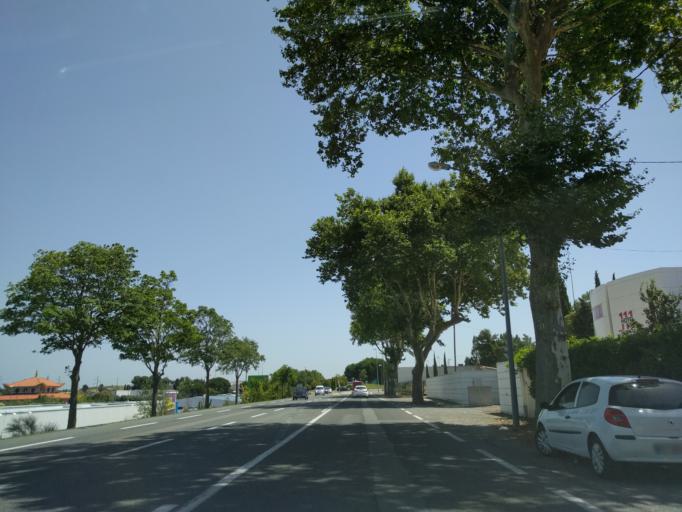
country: FR
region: Languedoc-Roussillon
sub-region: Departement de l'Aude
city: Cazilhac
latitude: 43.2072
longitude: 2.3816
